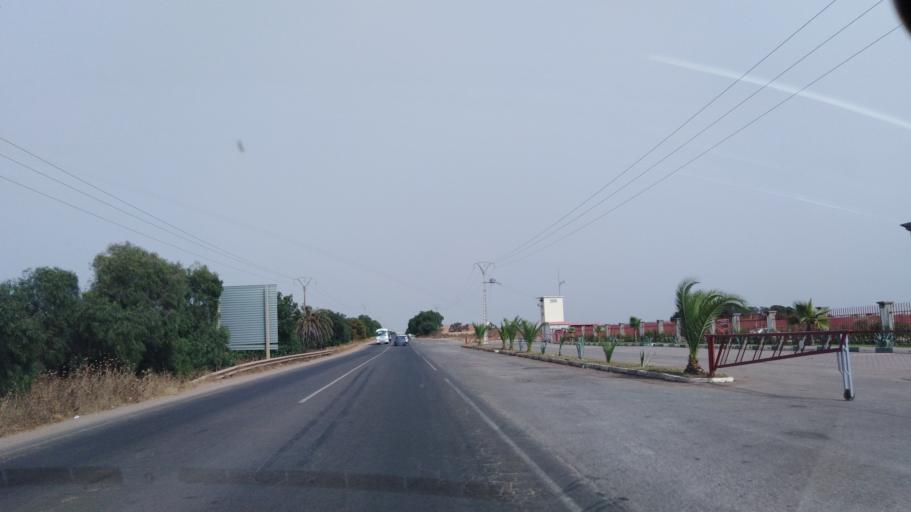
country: MA
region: Chaouia-Ouardigha
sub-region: Settat Province
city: Berrechid
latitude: 33.2469
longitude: -7.5573
